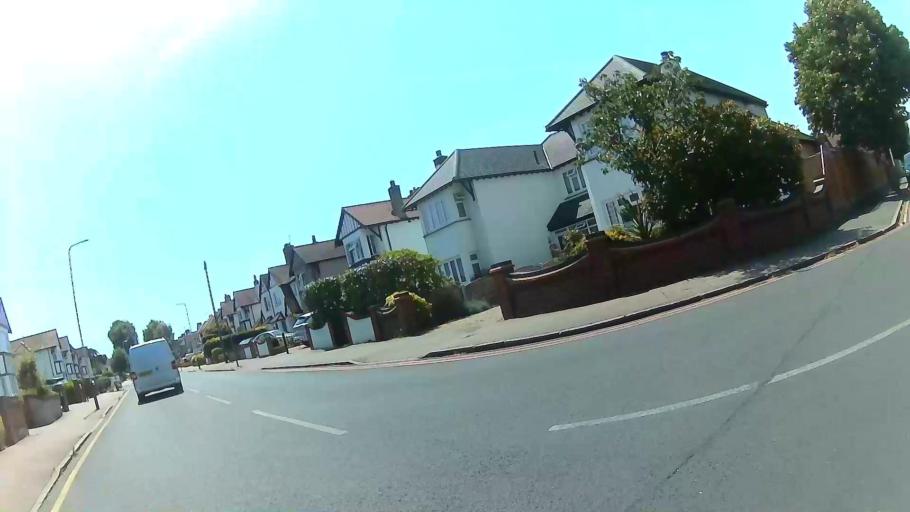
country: GB
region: England
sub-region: Greater London
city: Upminster
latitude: 51.5522
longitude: 0.2457
